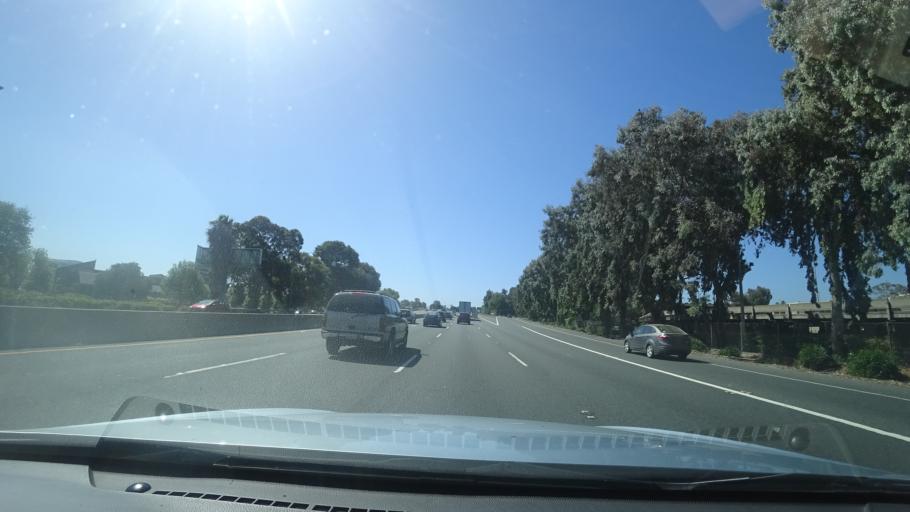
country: US
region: California
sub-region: Contra Costa County
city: Pleasant Hill
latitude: 37.9692
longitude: -122.0588
